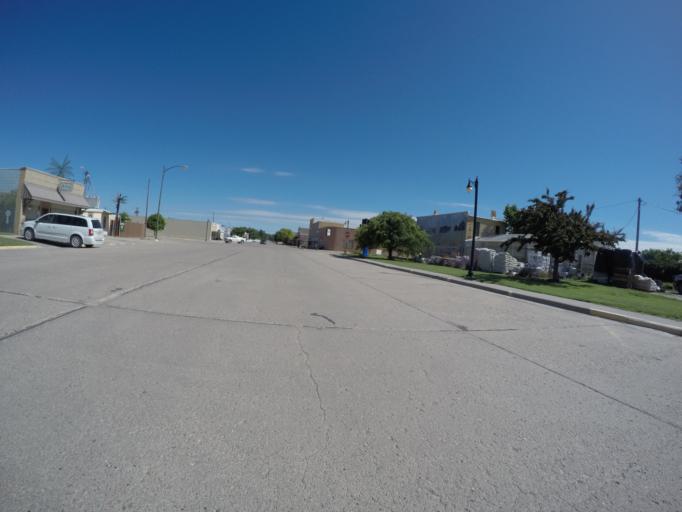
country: US
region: Kansas
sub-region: Rawlins County
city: Atwood
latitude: 39.8061
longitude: -101.0421
